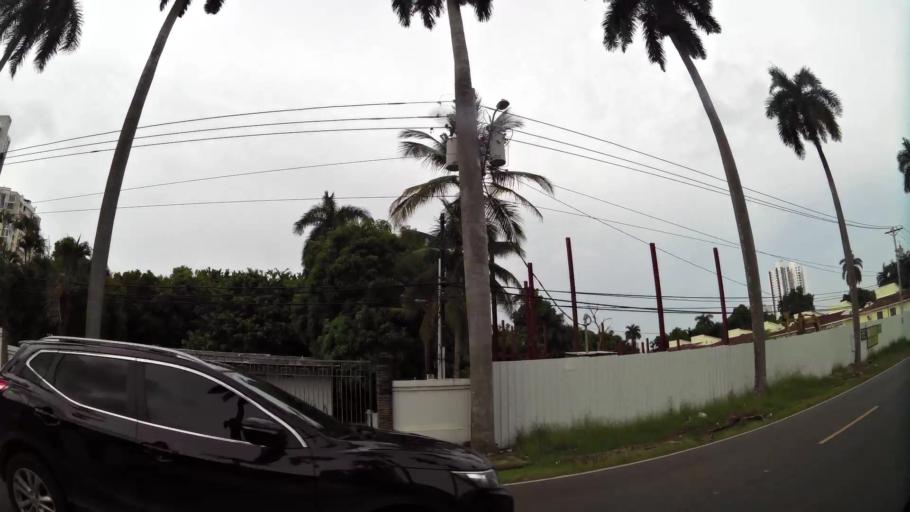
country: PA
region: Panama
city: Panama
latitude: 9.0033
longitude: -79.5038
